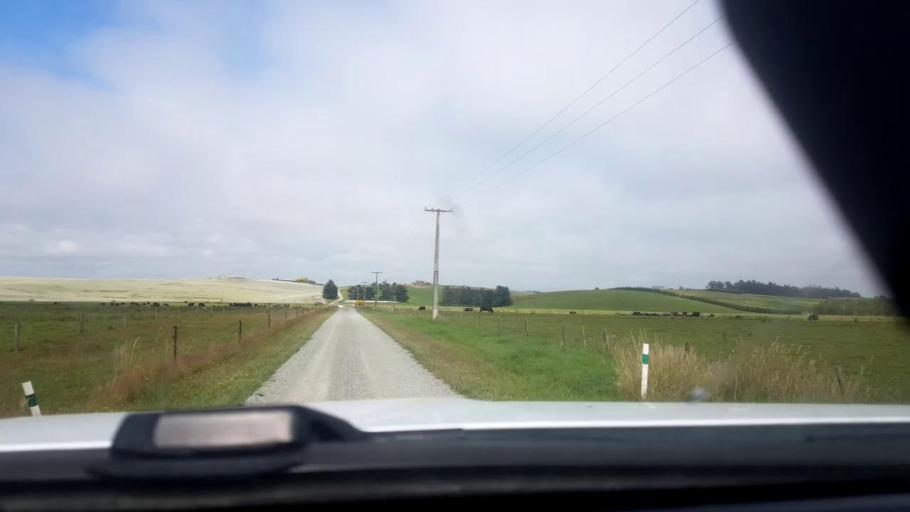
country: NZ
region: Canterbury
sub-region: Timaru District
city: Timaru
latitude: -44.3283
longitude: 171.2059
